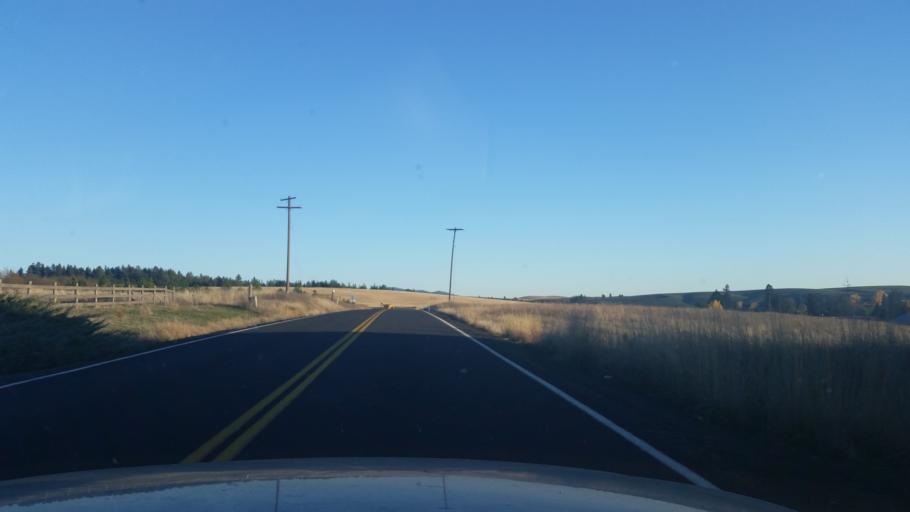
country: US
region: Washington
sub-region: Spokane County
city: Opportunity
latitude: 47.3498
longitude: -117.2304
